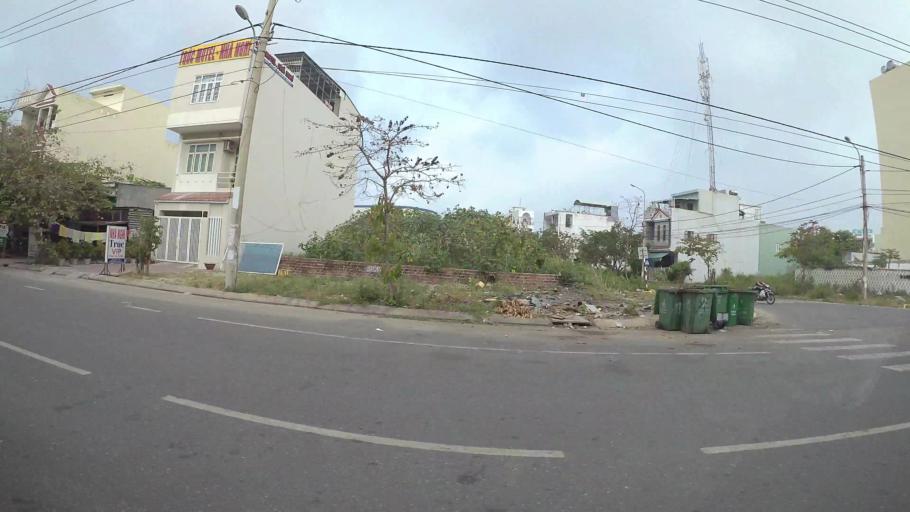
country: VN
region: Da Nang
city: Son Tra
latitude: 16.0833
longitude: 108.2452
